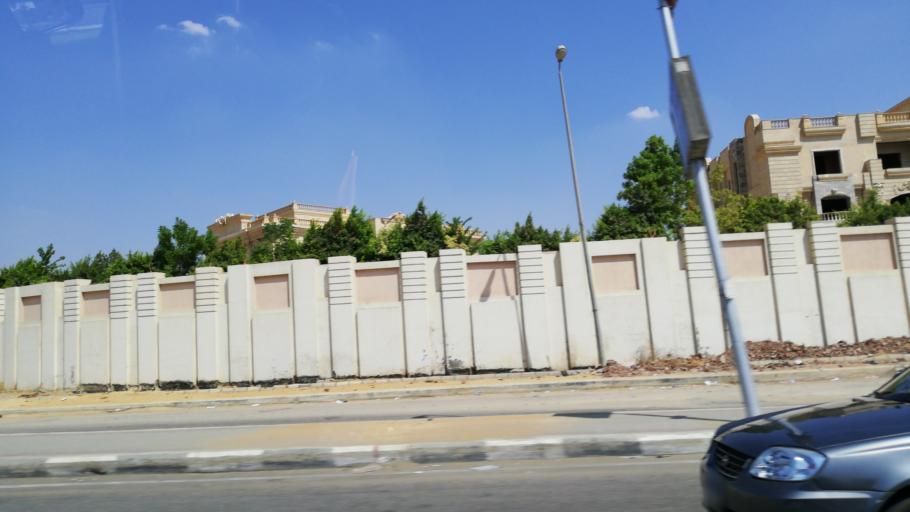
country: EG
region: Muhafazat al Qalyubiyah
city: Al Khankah
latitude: 30.0444
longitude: 31.4751
